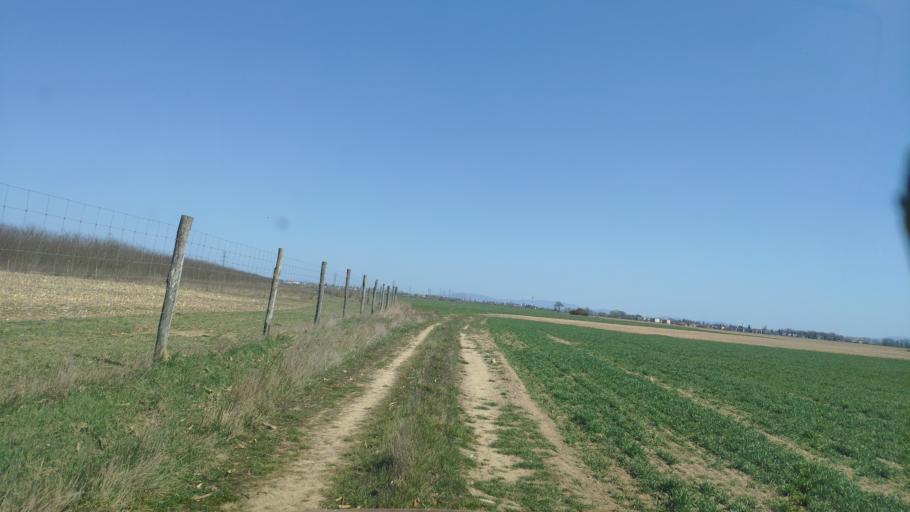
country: SK
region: Kosicky
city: Moldava nad Bodvou
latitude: 48.5937
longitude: 20.9652
